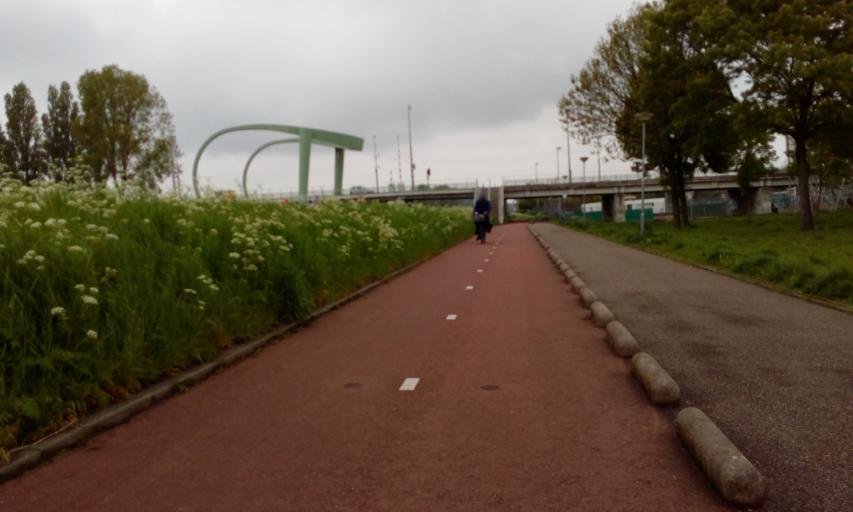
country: NL
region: South Holland
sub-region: Gemeente Schiedam
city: Schiedam
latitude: 51.9337
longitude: 4.4228
